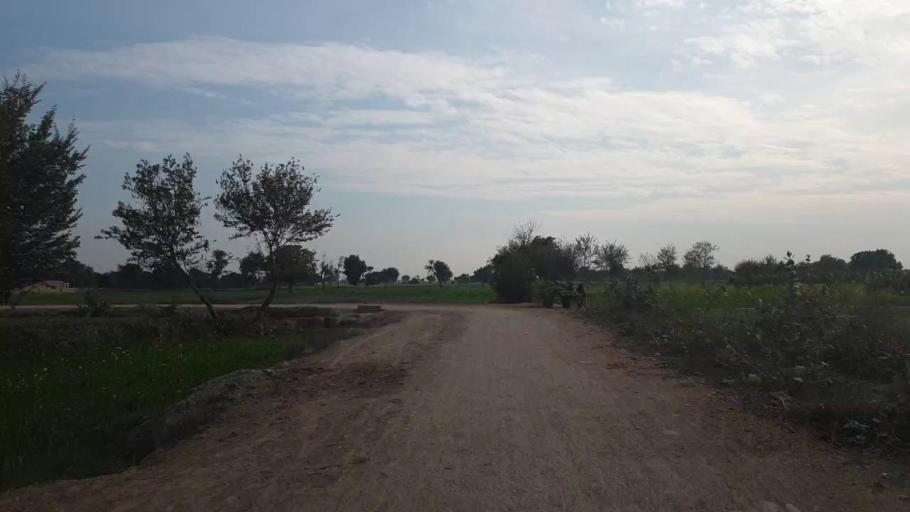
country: PK
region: Sindh
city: Shahdadpur
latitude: 26.0446
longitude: 68.5764
